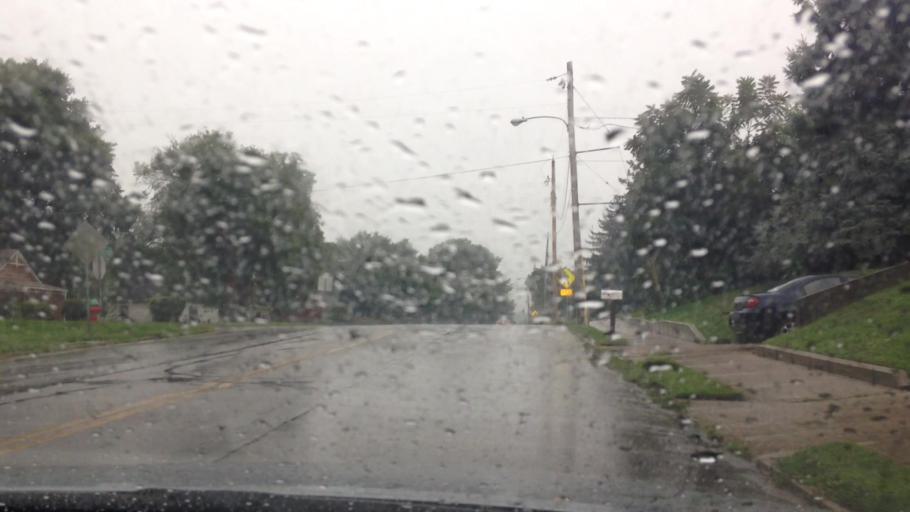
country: US
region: Kansas
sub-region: Leavenworth County
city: Leavenworth
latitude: 39.2953
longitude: -94.9184
